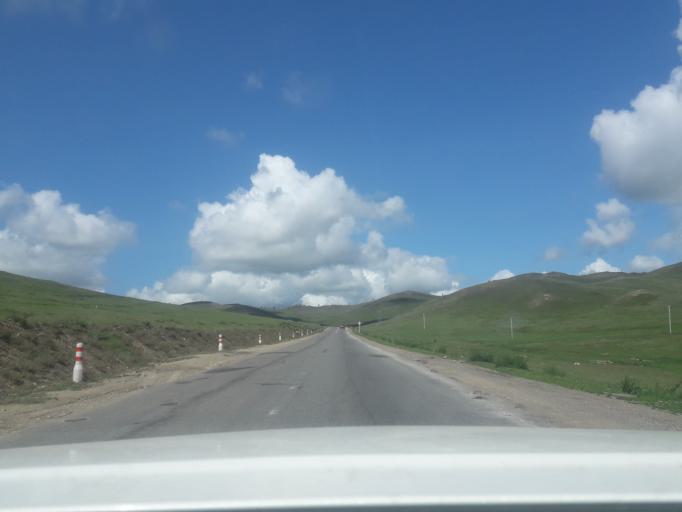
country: MN
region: Central Aimak
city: Ihsueuej
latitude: 48.1189
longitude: 106.4361
